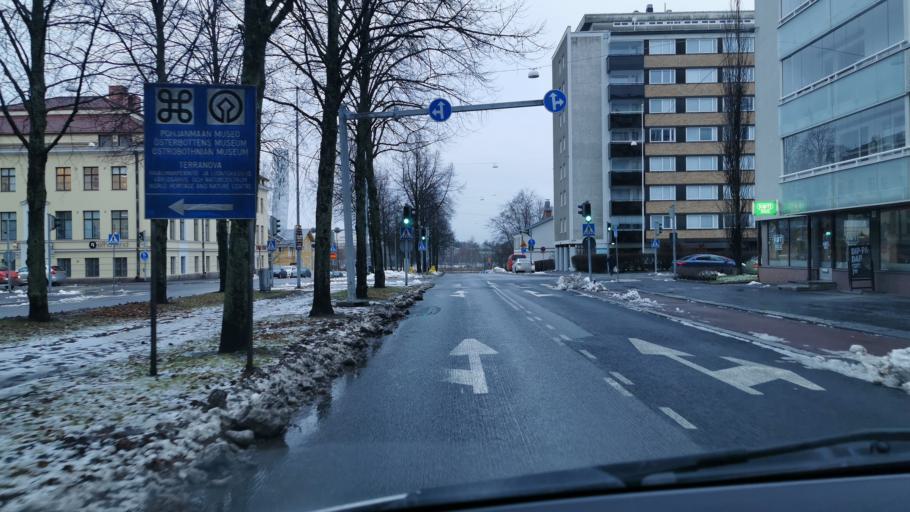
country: FI
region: Ostrobothnia
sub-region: Vaasa
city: Vaasa
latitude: 63.0994
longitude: 21.6062
